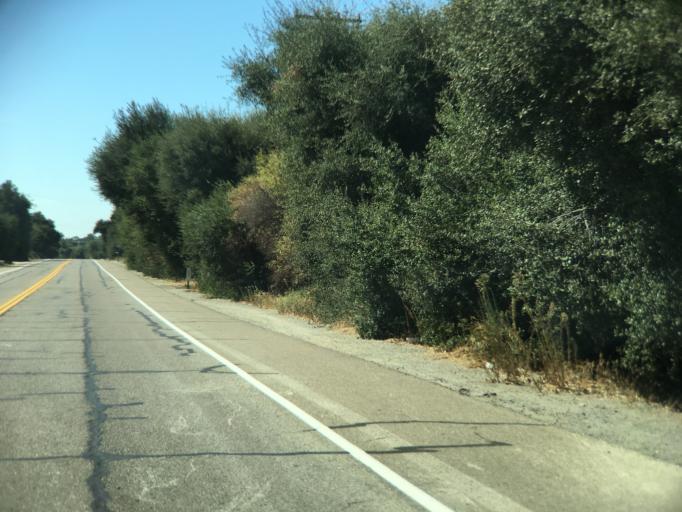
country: US
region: California
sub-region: San Diego County
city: Alpine
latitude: 32.8394
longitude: -116.7121
